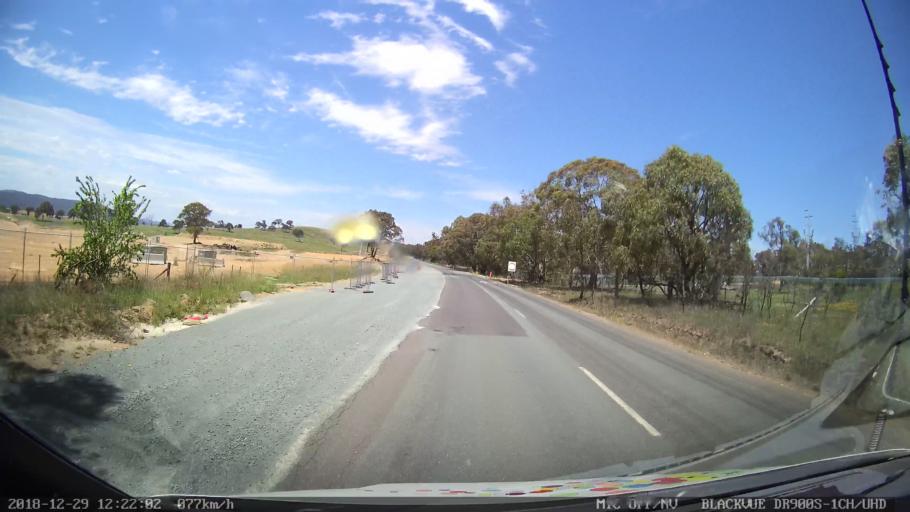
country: AU
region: New South Wales
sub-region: Queanbeyan
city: Queanbeyan
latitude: -35.4196
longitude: 149.2206
